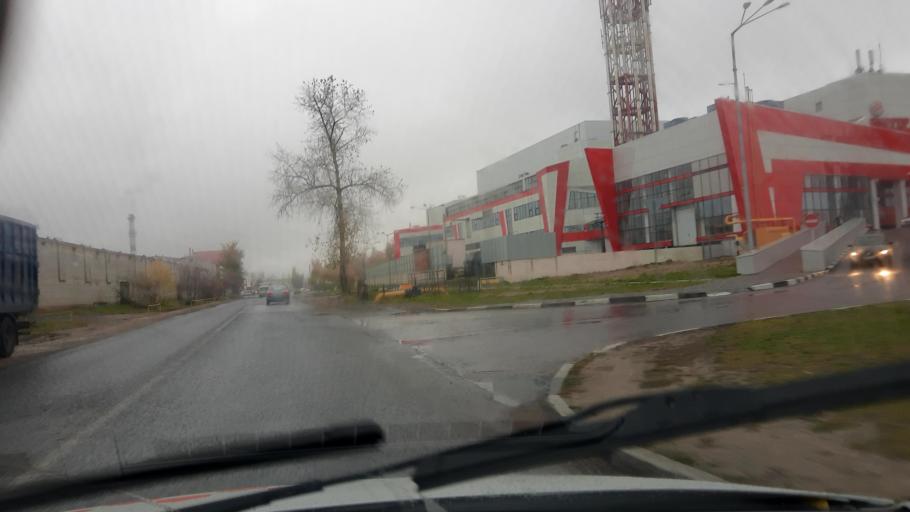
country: RU
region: Moskovskaya
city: Elektrostal'
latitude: 55.8135
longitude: 38.4278
